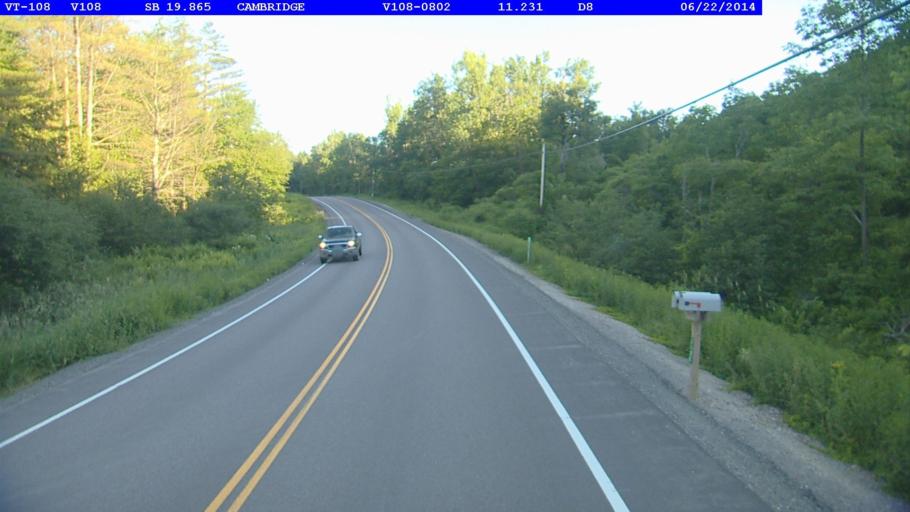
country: US
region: Vermont
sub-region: Lamoille County
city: Johnson
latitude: 44.6770
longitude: -72.8264
